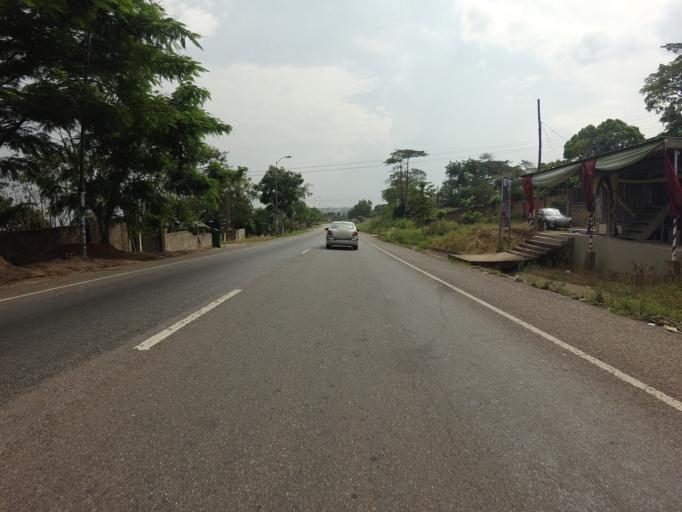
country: GH
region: Eastern
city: Aburi
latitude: 5.8290
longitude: -0.1846
